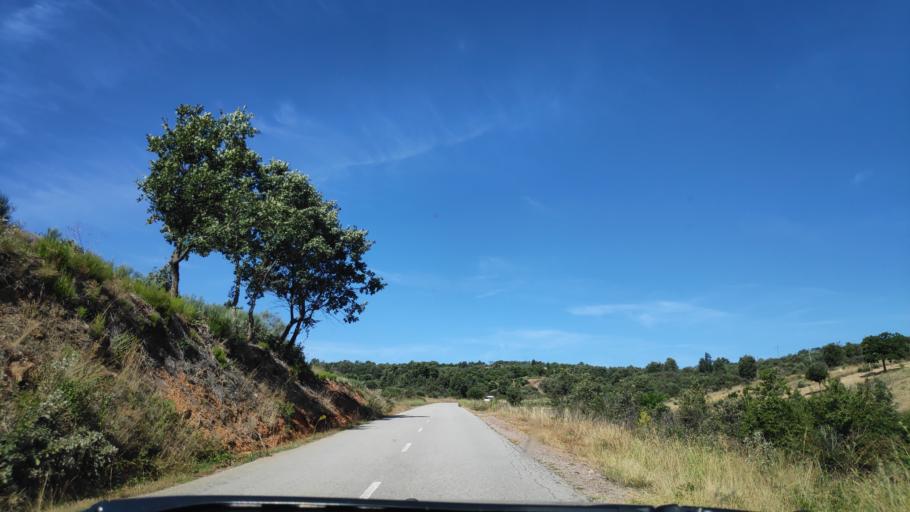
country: ES
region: Castille and Leon
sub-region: Provincia de Zamora
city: Alcanices
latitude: 41.6488
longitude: -6.3680
